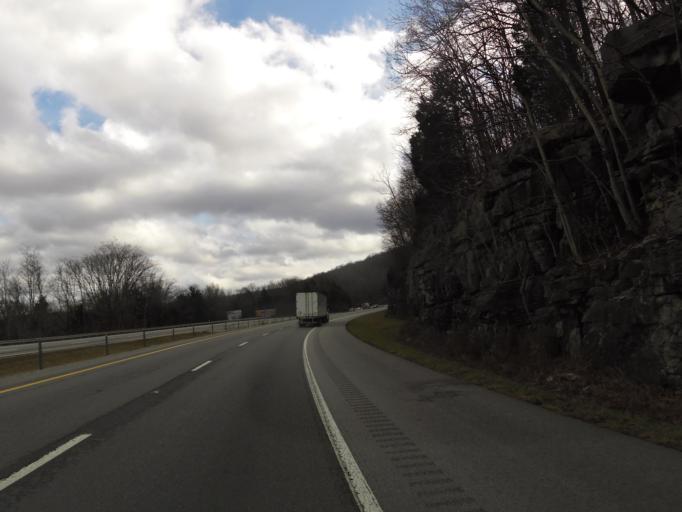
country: US
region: Tennessee
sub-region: Marion County
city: Monteagle
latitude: 35.2665
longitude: -85.8850
